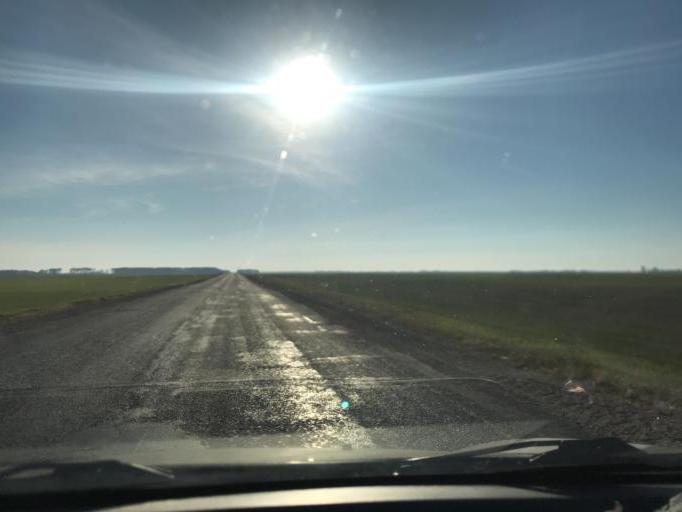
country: BY
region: Gomel
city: Khoyniki
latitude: 51.8295
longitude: 30.0605
